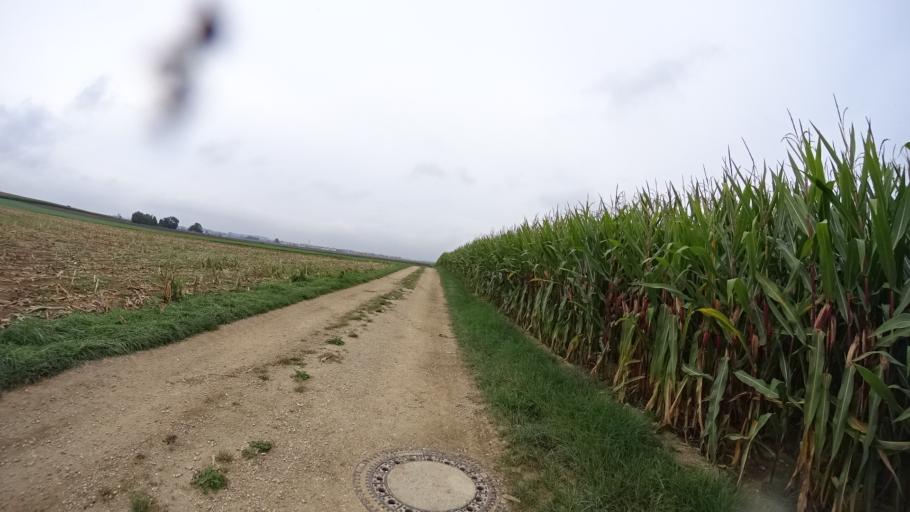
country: DE
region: Bavaria
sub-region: Upper Bavaria
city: Gaimersheim
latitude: 48.8296
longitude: 11.3581
